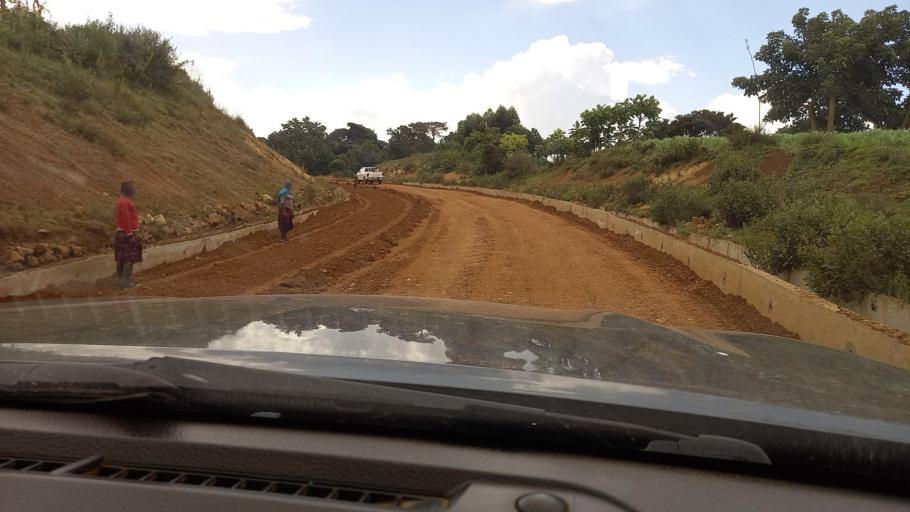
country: ET
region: Southern Nations, Nationalities, and People's Region
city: Mizan Teferi
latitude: 6.2179
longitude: 35.6354
